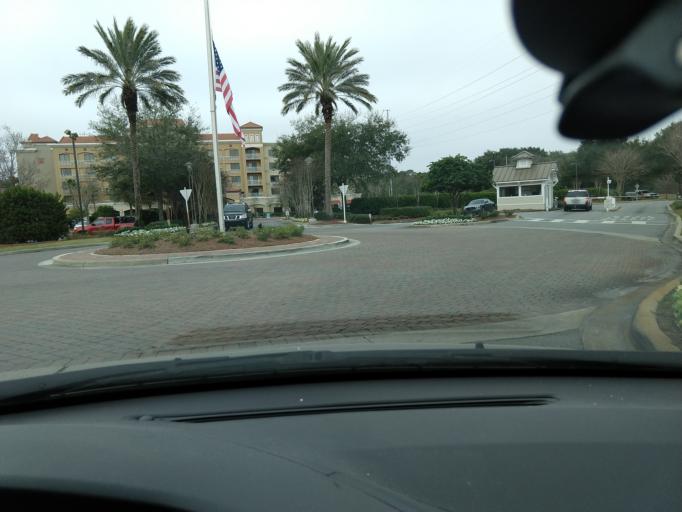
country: US
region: Florida
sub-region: Walton County
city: Miramar Beach
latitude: 30.3800
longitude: -86.3201
